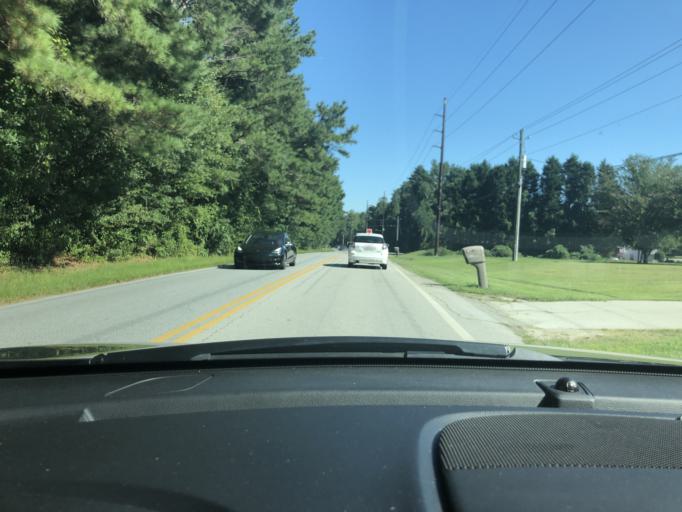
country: US
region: Georgia
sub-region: Gwinnett County
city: Grayson
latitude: 33.9148
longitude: -83.9361
